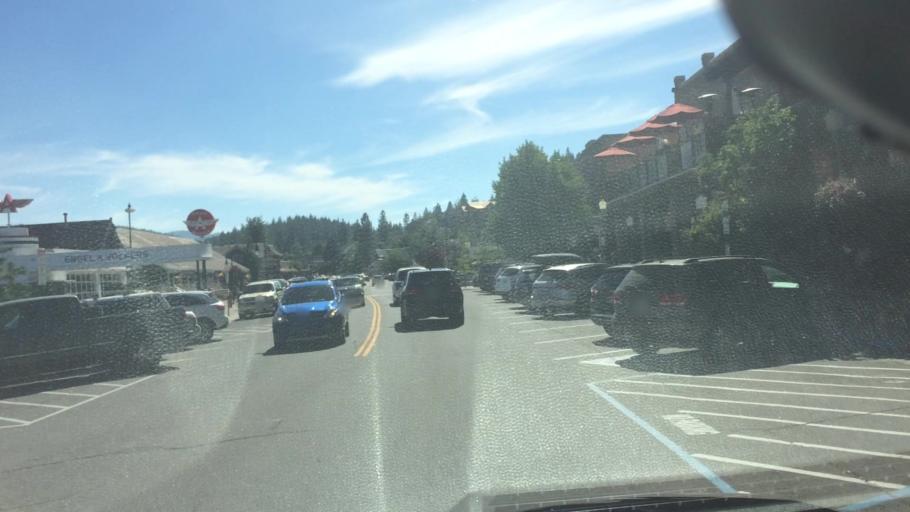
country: US
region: California
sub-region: Nevada County
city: Truckee
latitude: 39.3277
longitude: -120.1860
